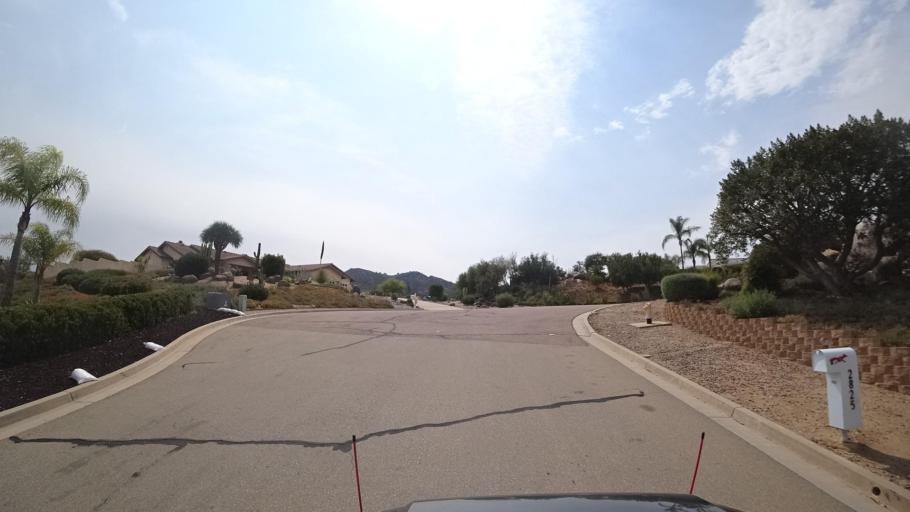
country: US
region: California
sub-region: San Diego County
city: Ramona
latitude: 32.9973
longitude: -116.8954
